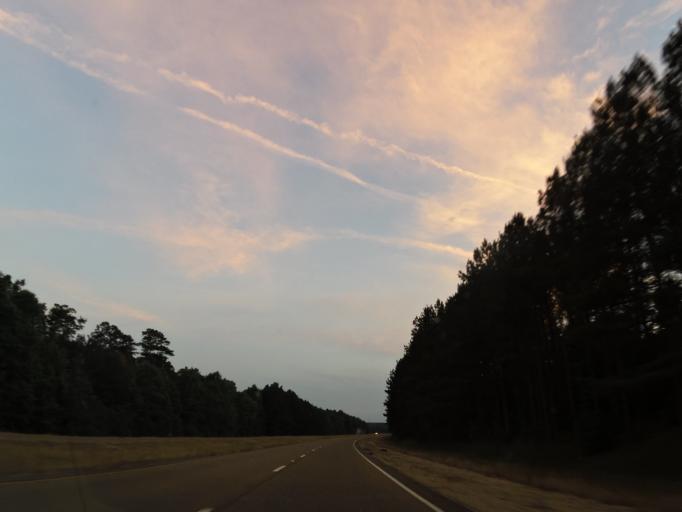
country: US
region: Mississippi
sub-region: Lauderdale County
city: Meridian Station
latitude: 32.6024
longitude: -88.4987
